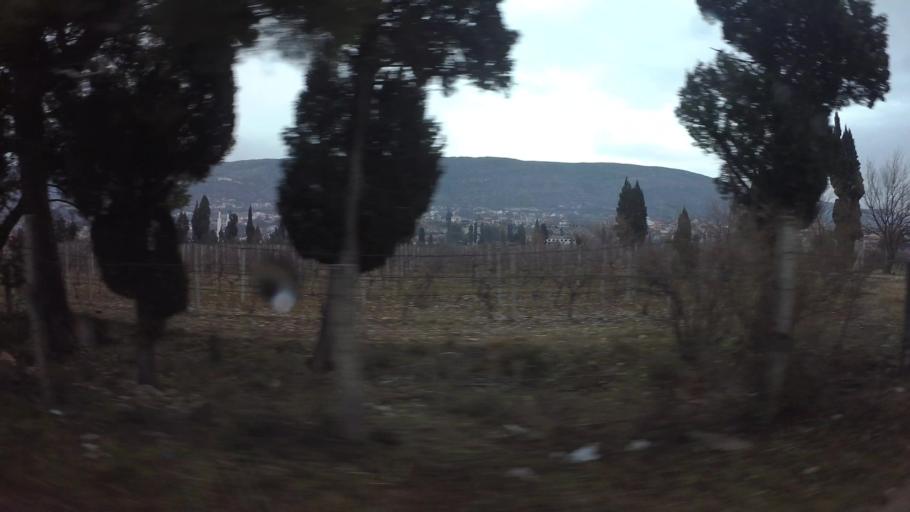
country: BA
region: Federation of Bosnia and Herzegovina
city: Rodoc
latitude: 43.2999
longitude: 17.8411
